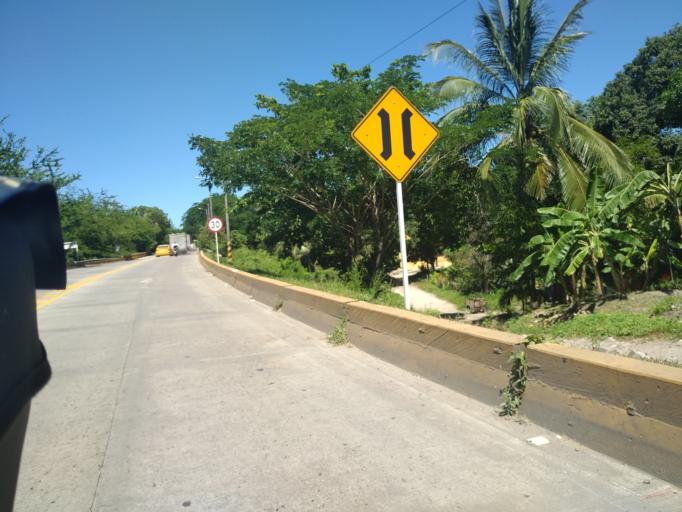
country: CO
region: Cundinamarca
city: Puerto Salgar
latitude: 5.4682
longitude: -74.6661
